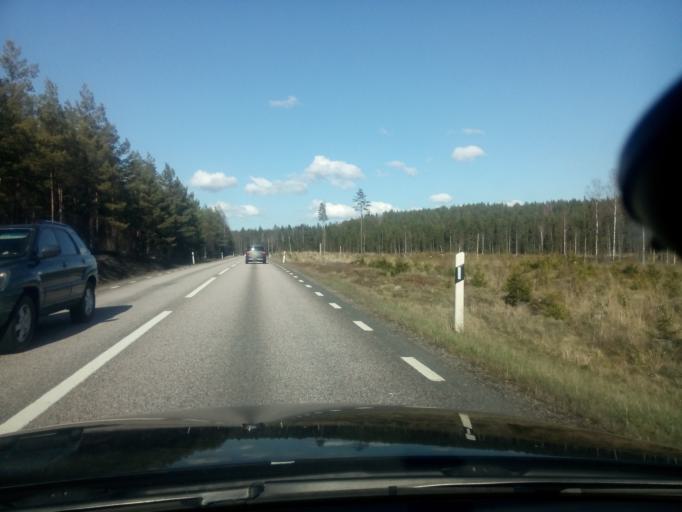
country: SE
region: Soedermanland
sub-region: Strangnas Kommun
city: Akers Styckebruk
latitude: 59.2235
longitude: 16.9167
